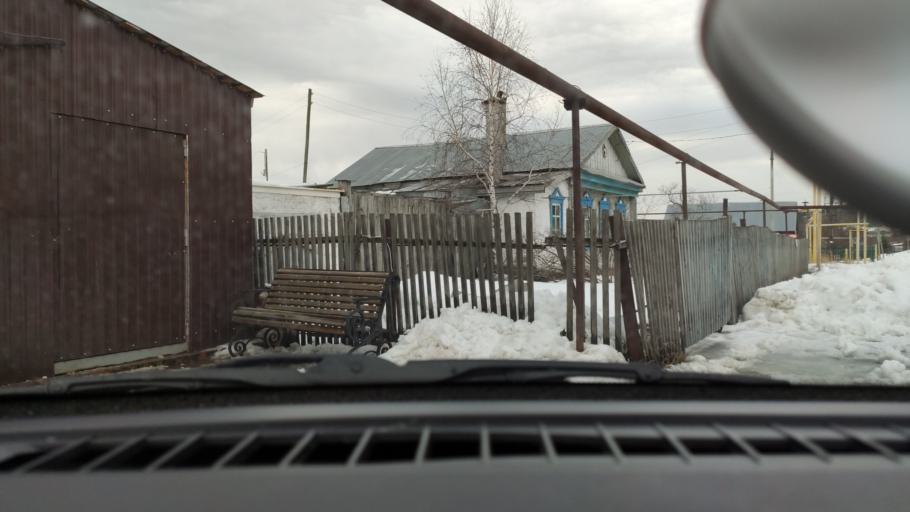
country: RU
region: Samara
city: Kurumoch
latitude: 53.4825
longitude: 50.0396
